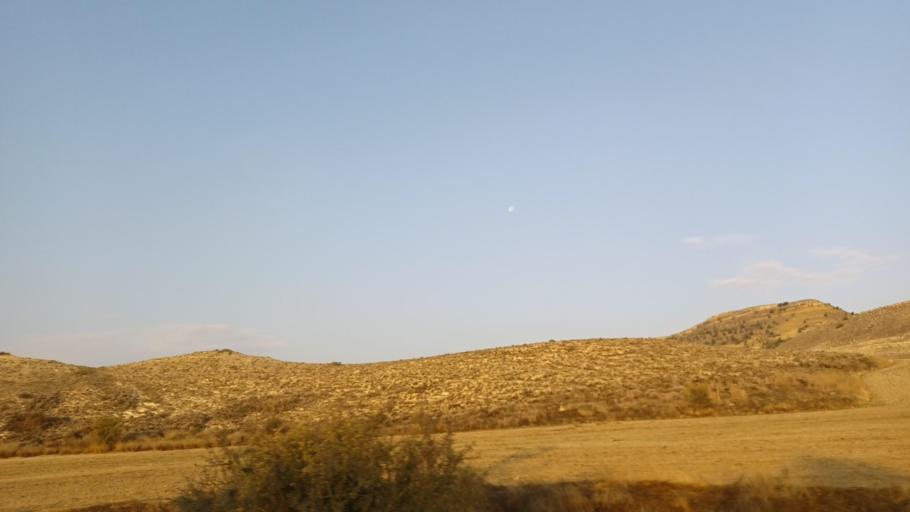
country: CY
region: Larnaka
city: Athienou
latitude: 35.0057
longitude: 33.5245
